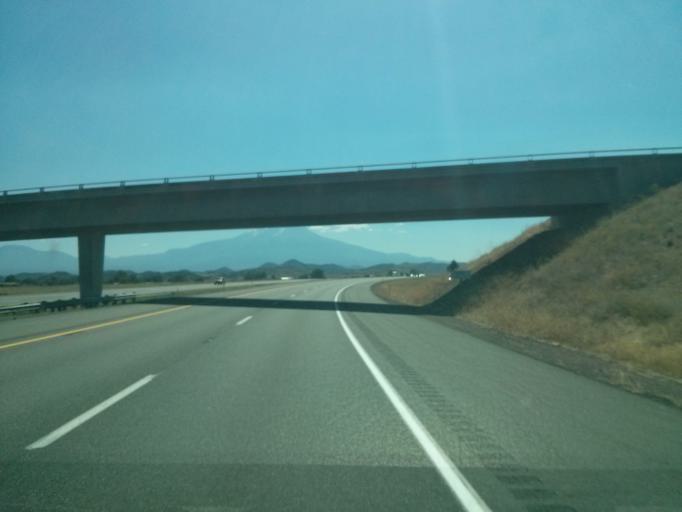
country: US
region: California
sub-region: Siskiyou County
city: Montague
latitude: 41.6463
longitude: -122.5358
